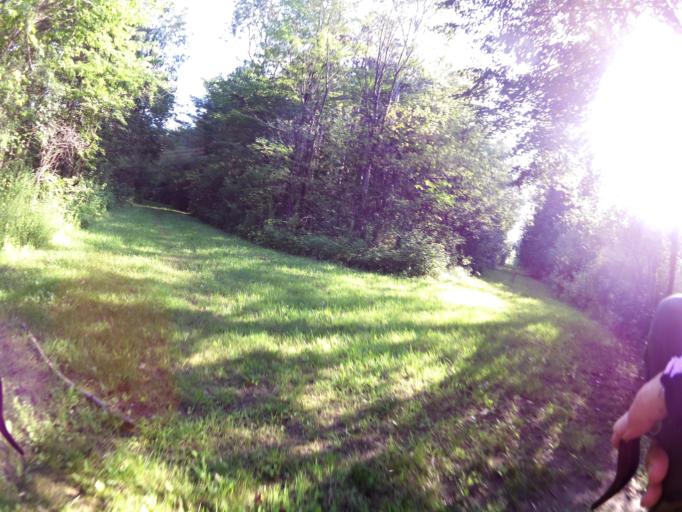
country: CA
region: Ontario
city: Bells Corners
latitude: 45.3152
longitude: -75.7339
